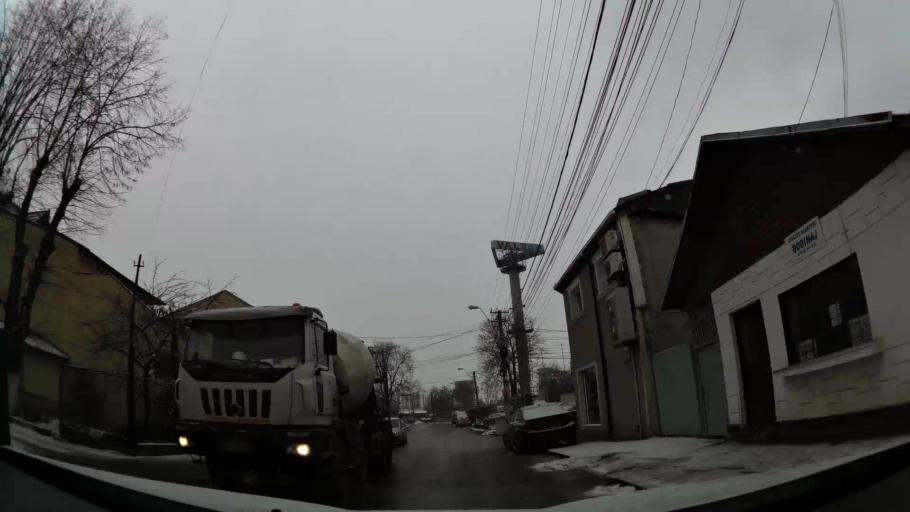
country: RO
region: Prahova
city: Ploiesti
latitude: 44.9264
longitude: 26.0246
